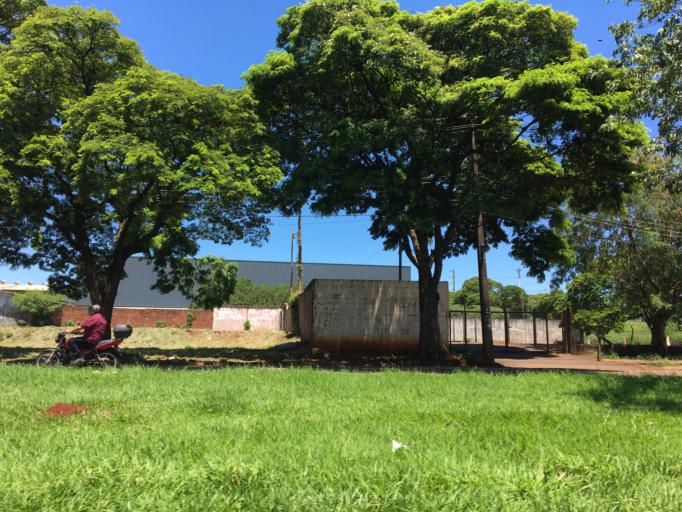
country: BR
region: Parana
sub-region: Maringa
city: Maringa
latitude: -23.4477
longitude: -51.9806
